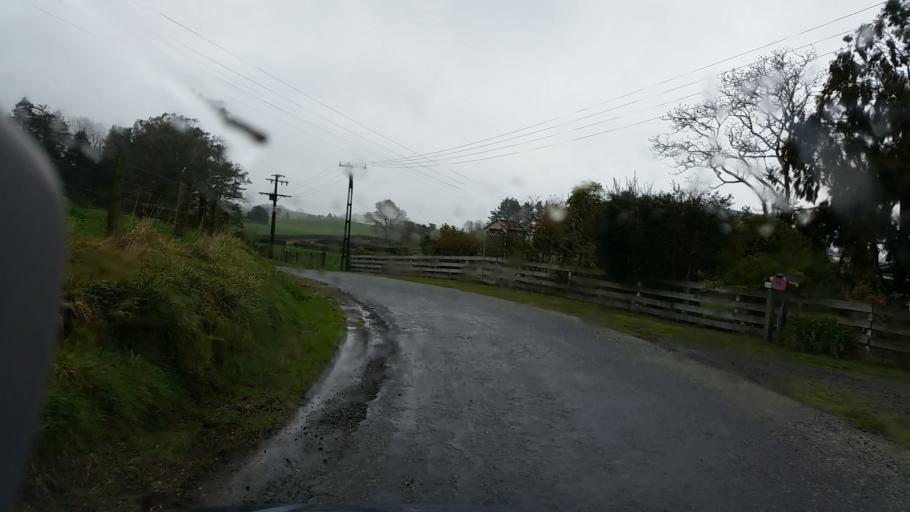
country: NZ
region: Taranaki
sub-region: South Taranaki District
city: Eltham
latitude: -39.2835
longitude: 174.3379
